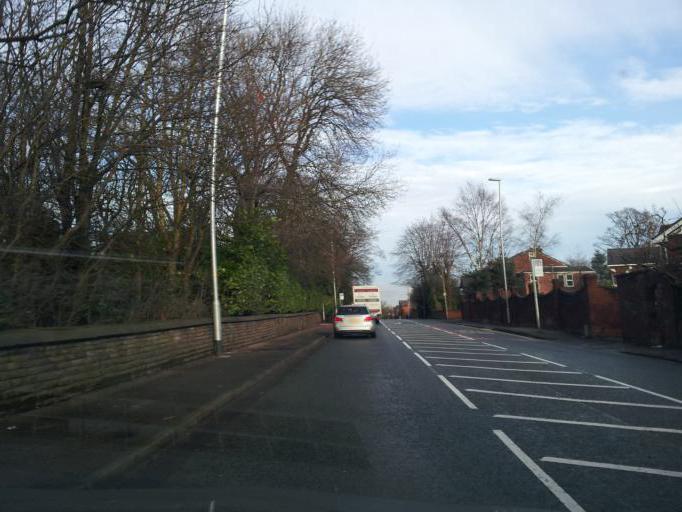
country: GB
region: England
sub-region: Manchester
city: Heywood
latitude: 53.5802
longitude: -2.2141
